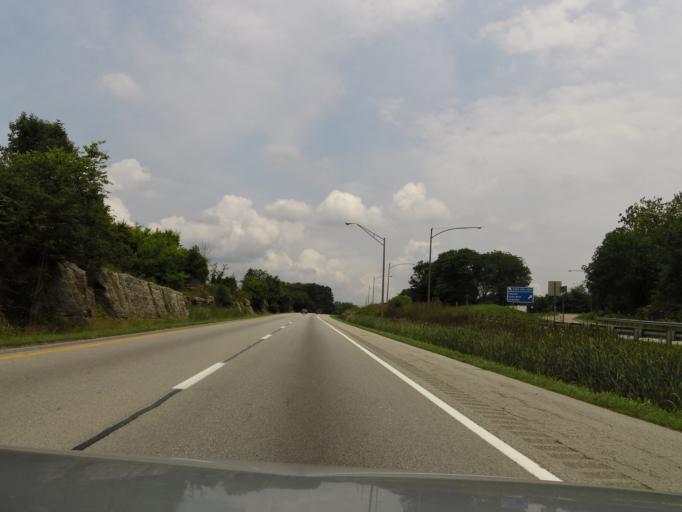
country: US
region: Kentucky
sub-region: Oldham County
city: Orchard Grass Hills
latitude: 38.3376
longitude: -85.5194
